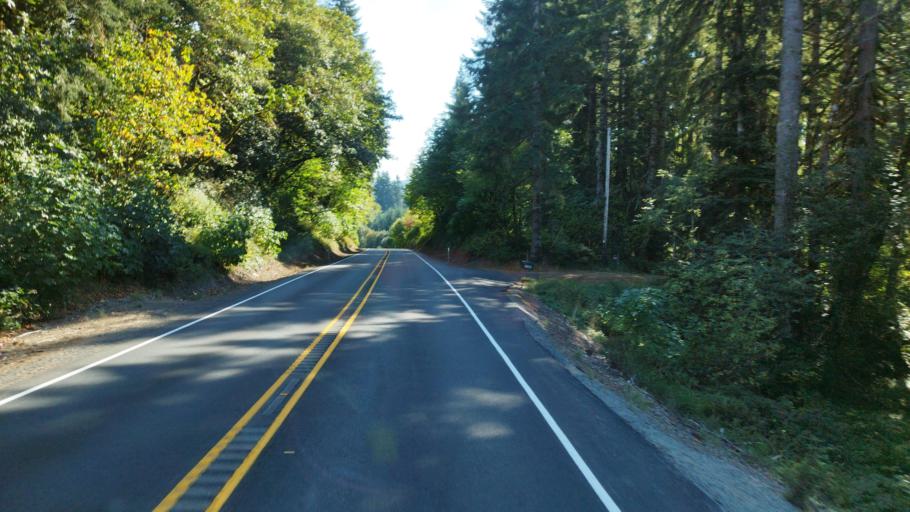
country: US
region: Oregon
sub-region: Clatsop County
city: Seaside
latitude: 45.8740
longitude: -123.6018
